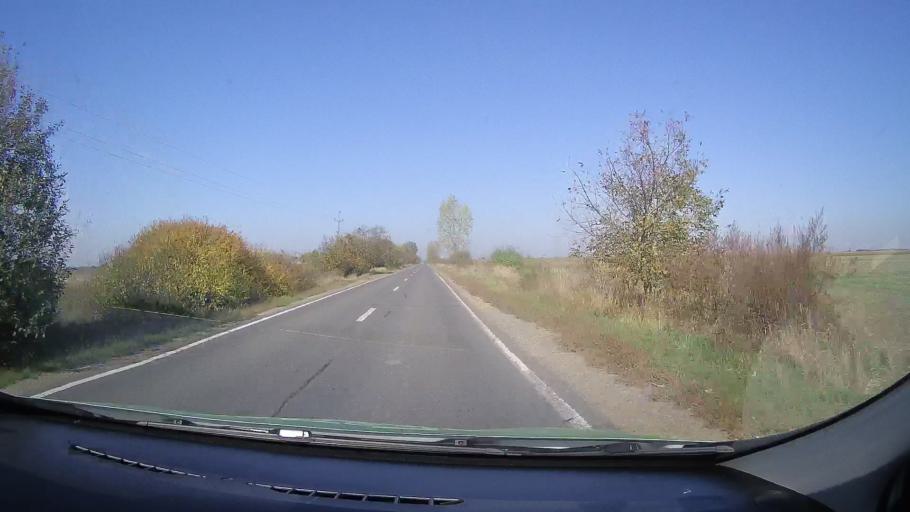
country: RO
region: Satu Mare
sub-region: Comuna Urziceni
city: Urziceni
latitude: 47.7187
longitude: 22.4184
